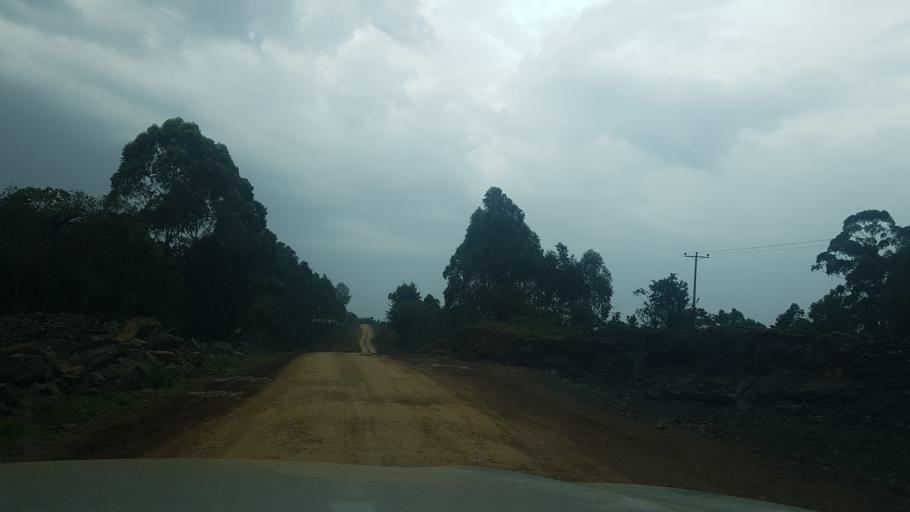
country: ET
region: Oromiya
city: Gore
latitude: 7.9135
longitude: 35.5131
